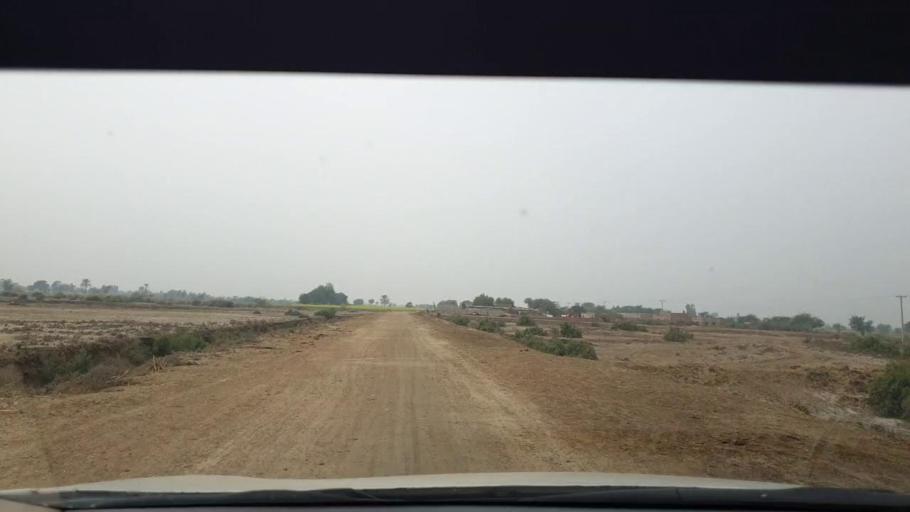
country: PK
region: Sindh
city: Berani
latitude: 25.8288
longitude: 68.8477
